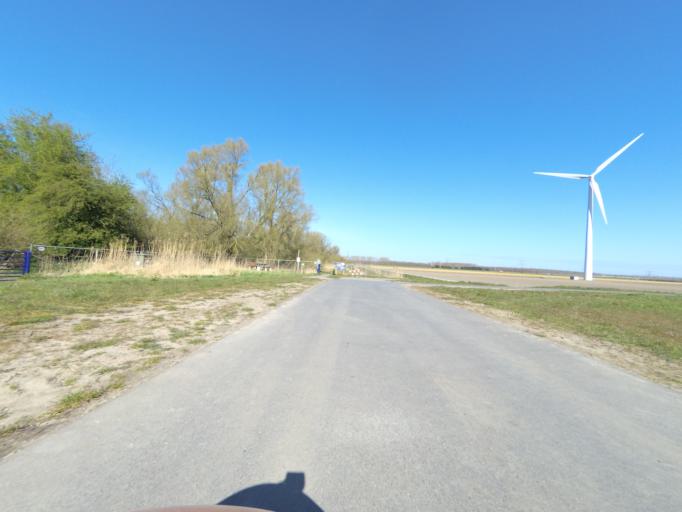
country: NL
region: Flevoland
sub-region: Gemeente Lelystad
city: Lelystad
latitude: 52.4323
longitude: 5.4356
